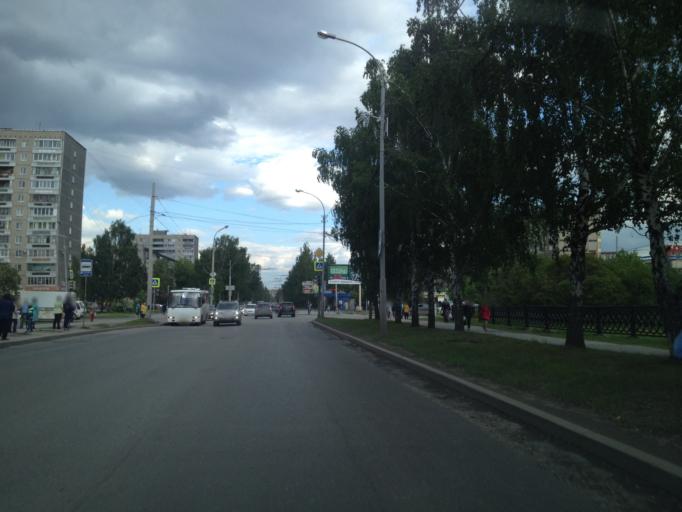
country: RU
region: Sverdlovsk
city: Sovkhoznyy
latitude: 56.8026
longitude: 60.5663
